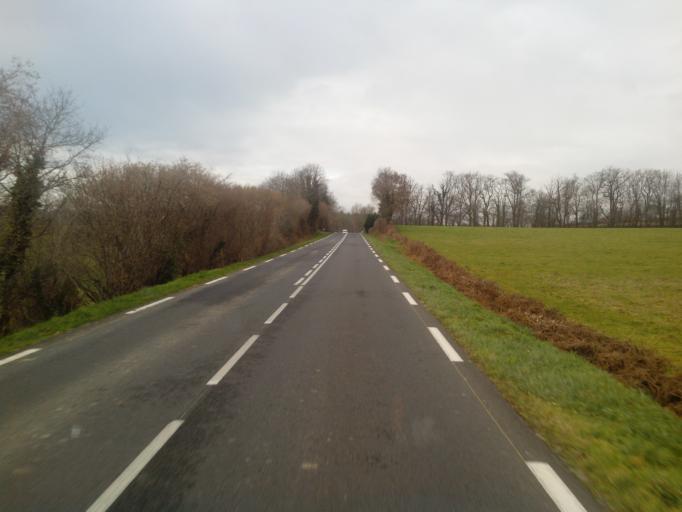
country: FR
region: Limousin
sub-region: Departement de la Haute-Vienne
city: Magnac-Laval
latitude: 46.2149
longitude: 1.1304
